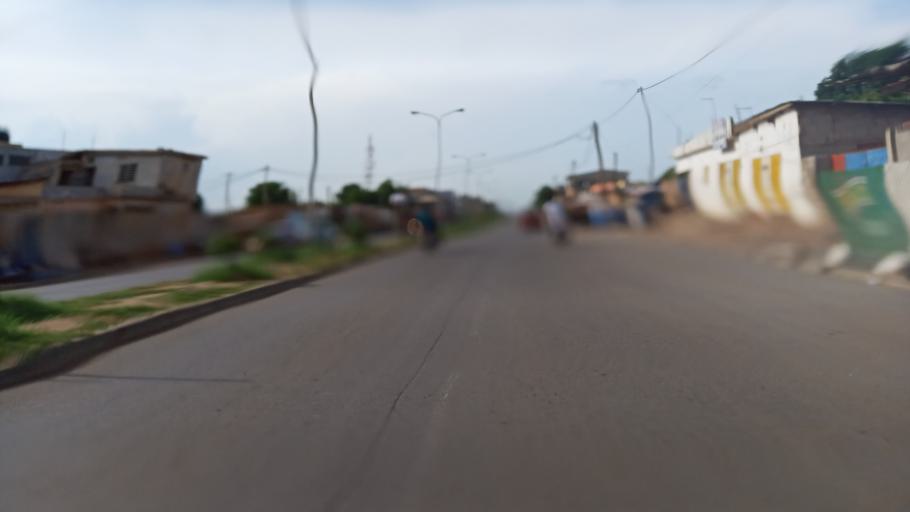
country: TG
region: Maritime
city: Lome
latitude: 6.1701
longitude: 1.2671
